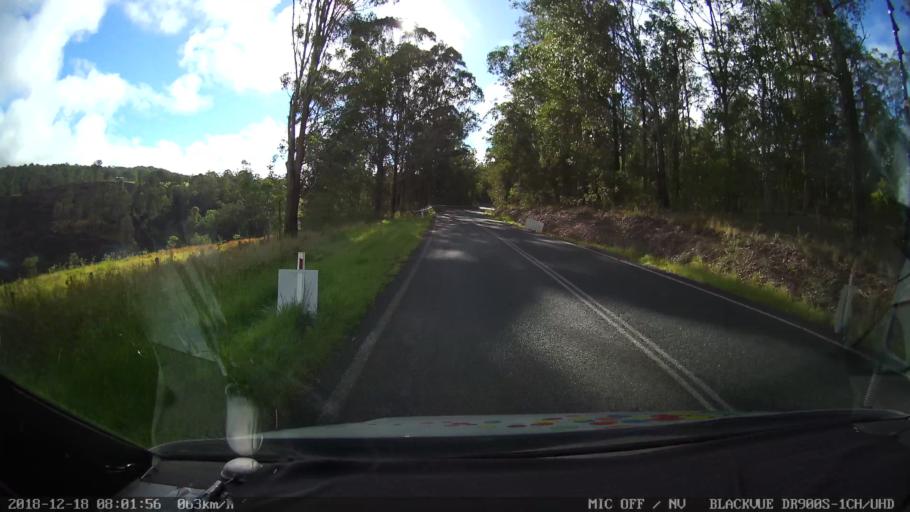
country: AU
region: New South Wales
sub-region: Kyogle
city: Kyogle
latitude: -28.3913
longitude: 152.6278
